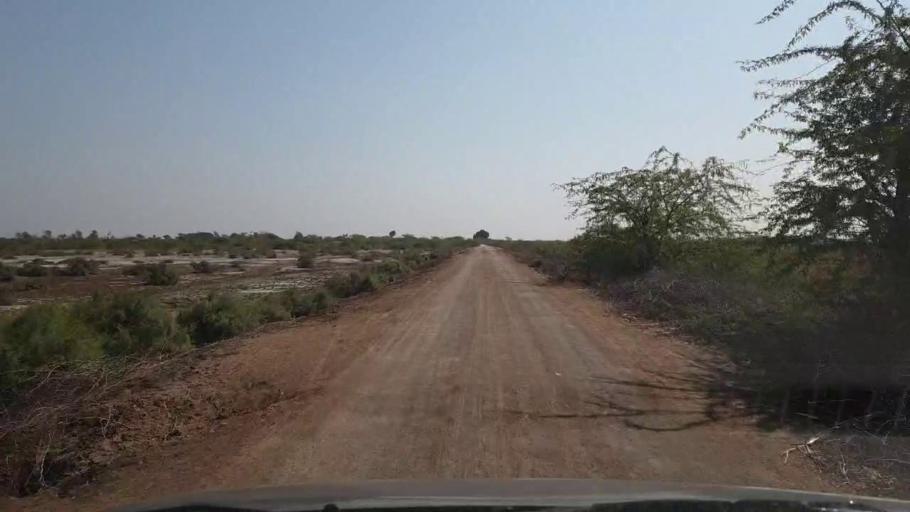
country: PK
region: Sindh
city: Samaro
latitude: 25.2483
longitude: 69.2842
